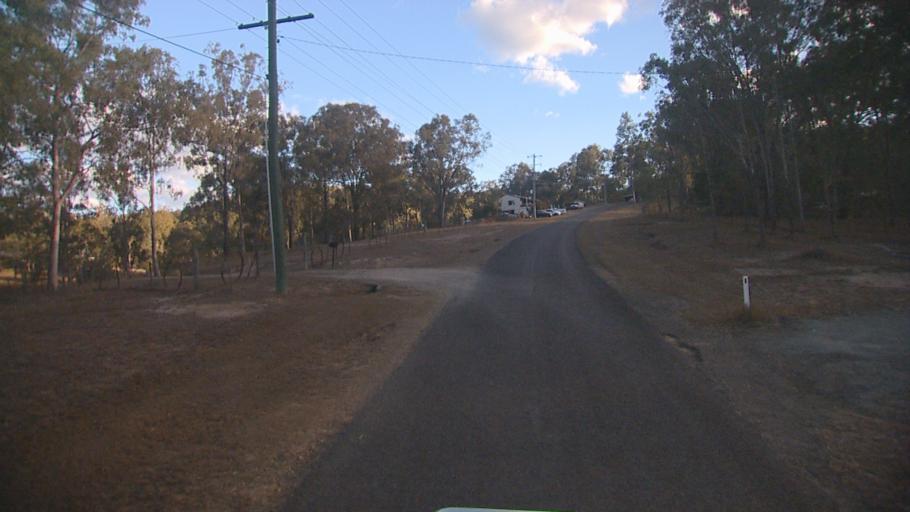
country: AU
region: Queensland
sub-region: Logan
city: Cedar Vale
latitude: -27.8479
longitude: 153.0817
